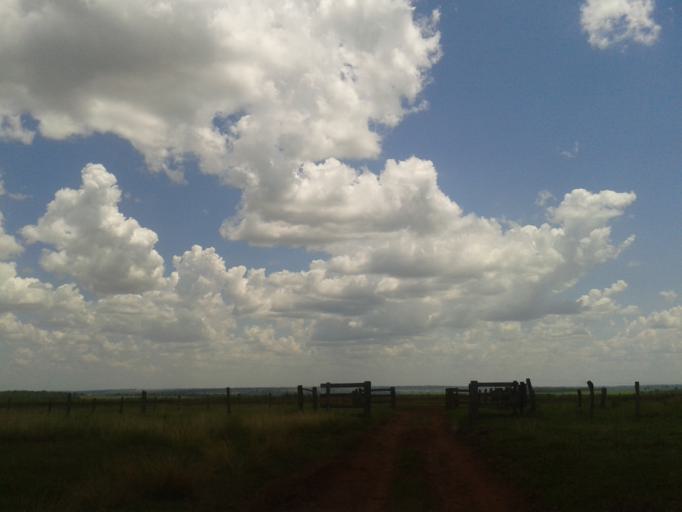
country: BR
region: Minas Gerais
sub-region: Santa Vitoria
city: Santa Vitoria
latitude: -19.1629
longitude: -50.4216
